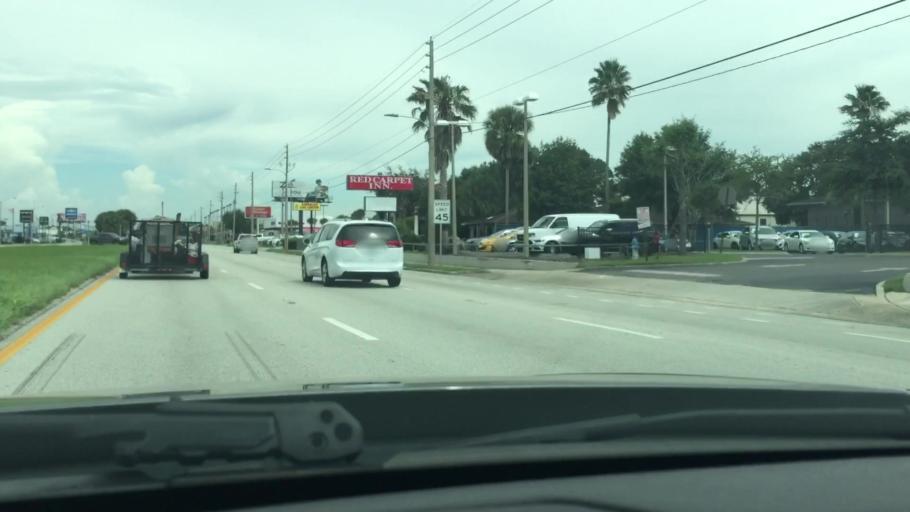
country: US
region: Florida
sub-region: Orange County
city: Pine Hills
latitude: 28.5526
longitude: -81.4289
